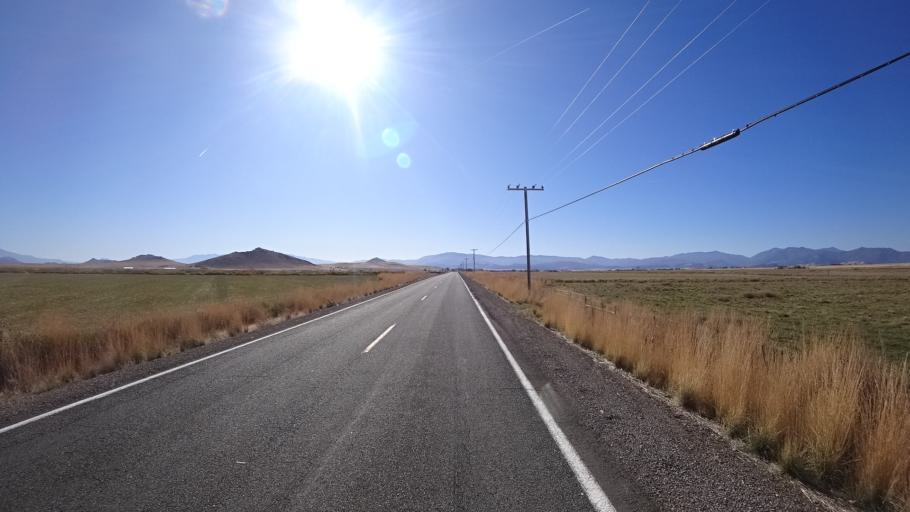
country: US
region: California
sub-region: Siskiyou County
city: Montague
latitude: 41.7647
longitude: -122.4870
